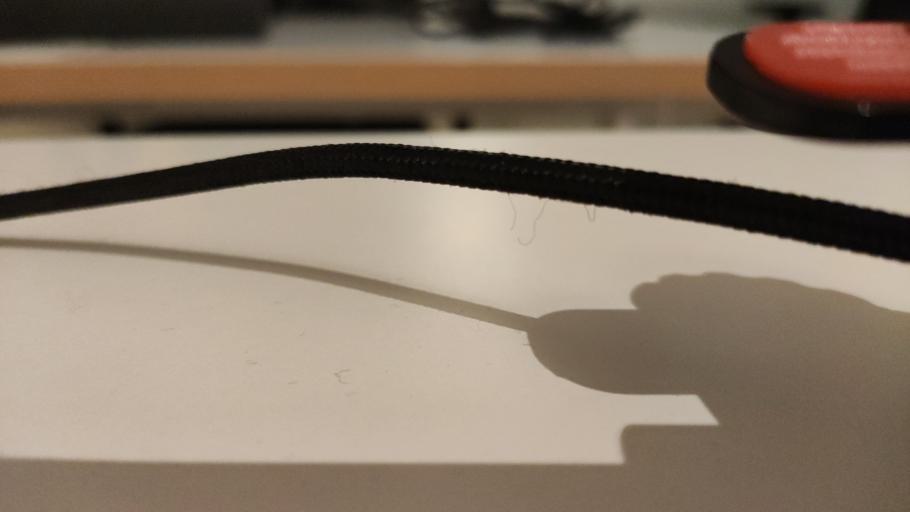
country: RU
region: Moskovskaya
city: Novoye
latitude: 55.6580
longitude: 38.9381
